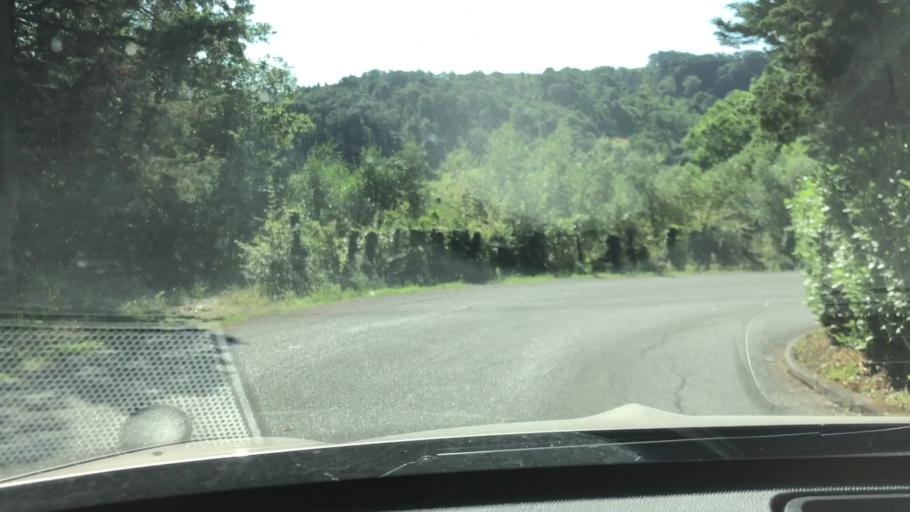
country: IT
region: Tuscany
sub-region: Province of Pisa
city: Forcoli
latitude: 43.6066
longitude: 10.7056
